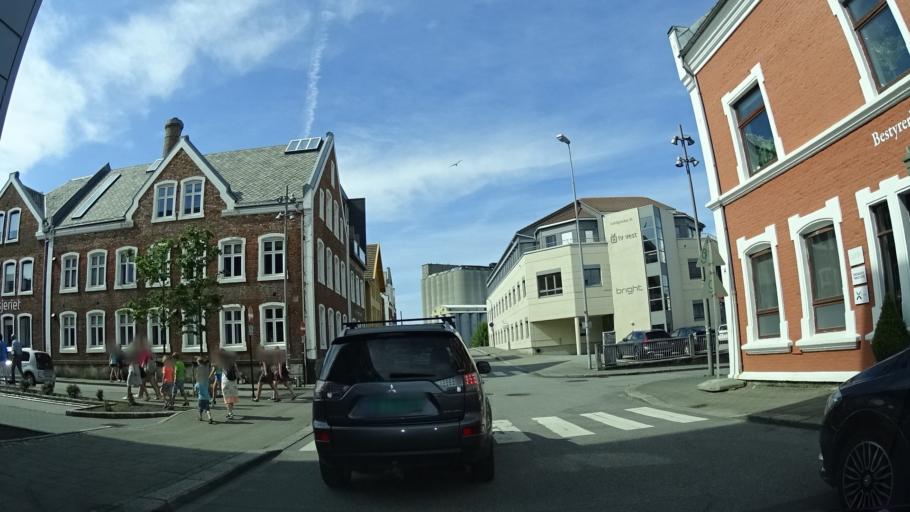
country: NO
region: Rogaland
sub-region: Stavanger
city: Stavanger
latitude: 58.9691
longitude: 5.7573
